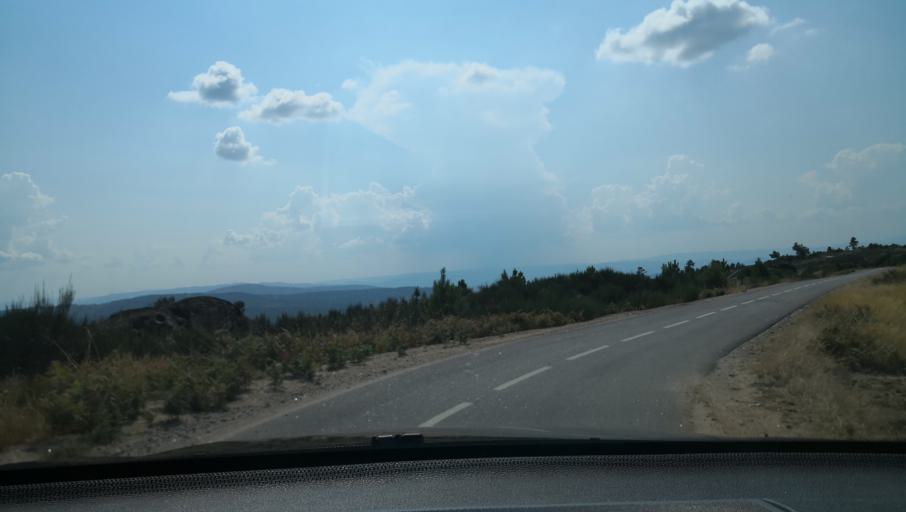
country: PT
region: Vila Real
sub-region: Sabrosa
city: Sabrosa
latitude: 41.2846
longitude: -7.6130
